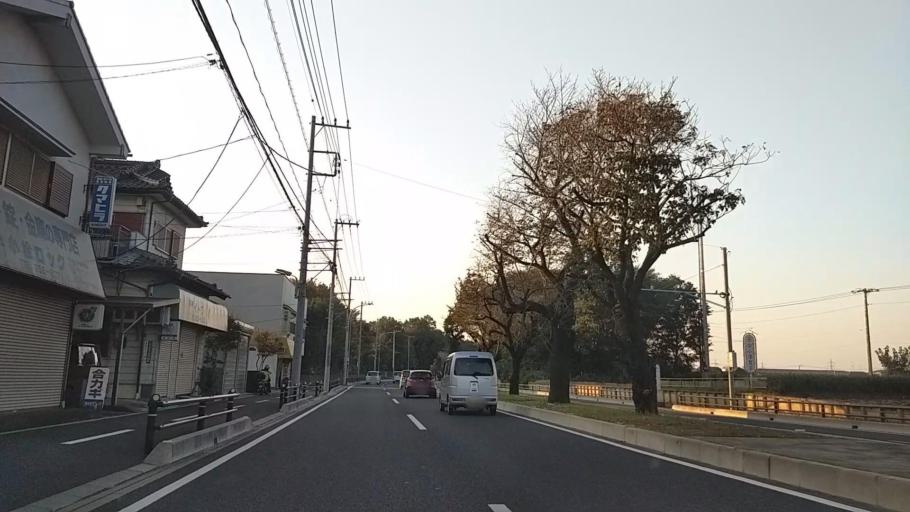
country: JP
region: Saitama
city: Sayama
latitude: 35.8527
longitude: 139.4375
